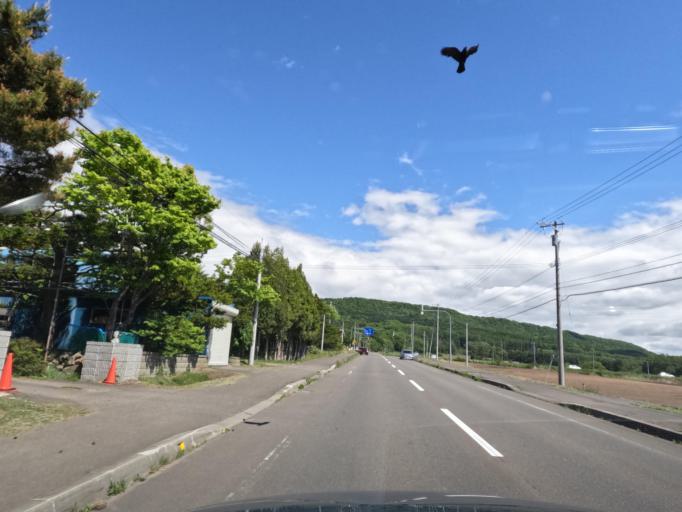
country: JP
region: Hokkaido
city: Kitahiroshima
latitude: 42.9973
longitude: 141.7278
